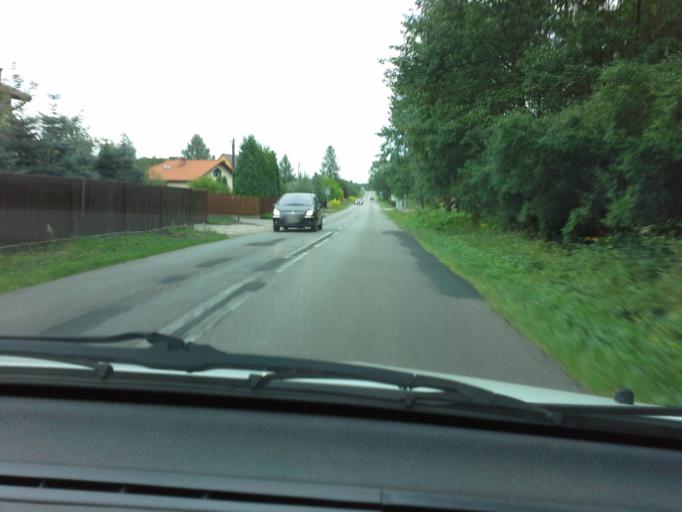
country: PL
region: Lesser Poland Voivodeship
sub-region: Powiat chrzanowski
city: Plaza
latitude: 50.1211
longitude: 19.4474
